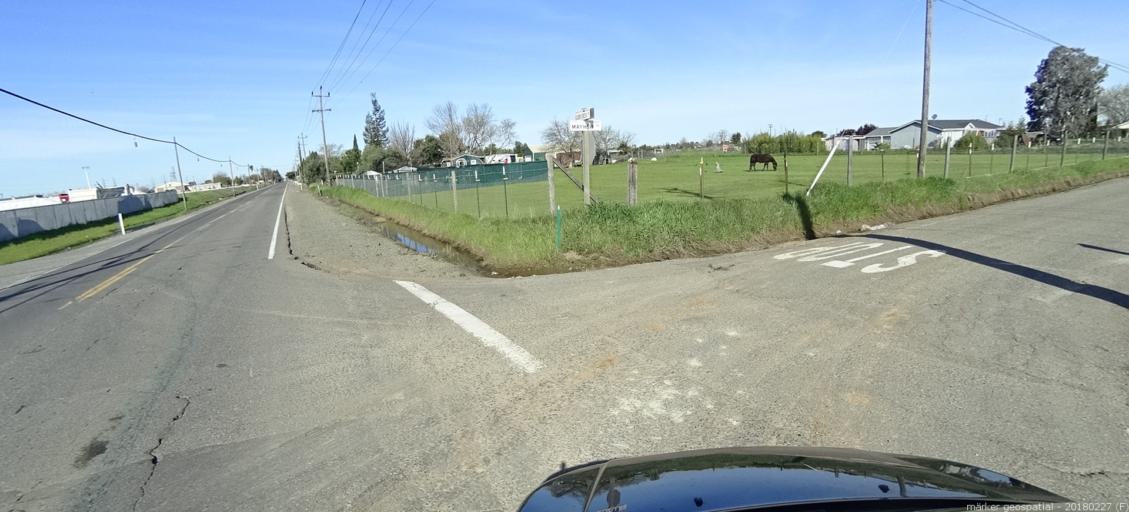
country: US
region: California
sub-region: Sacramento County
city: Rosemont
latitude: 38.5108
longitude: -121.3441
